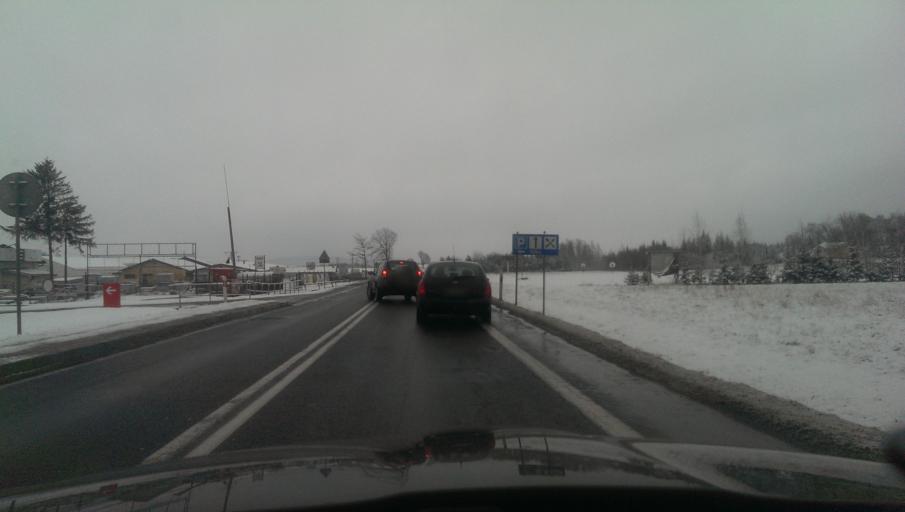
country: PL
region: Subcarpathian Voivodeship
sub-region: Powiat krosnienski
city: Rymanow
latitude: 49.5747
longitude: 21.8755
